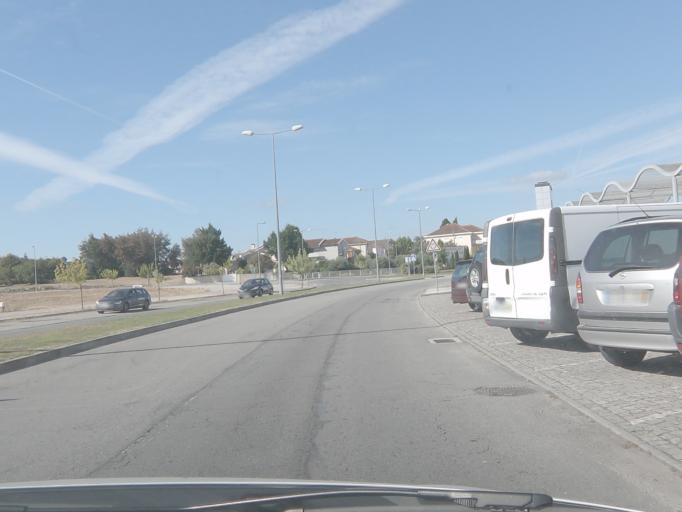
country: PT
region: Viseu
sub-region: Viseu
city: Viseu
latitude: 40.6378
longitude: -7.9287
